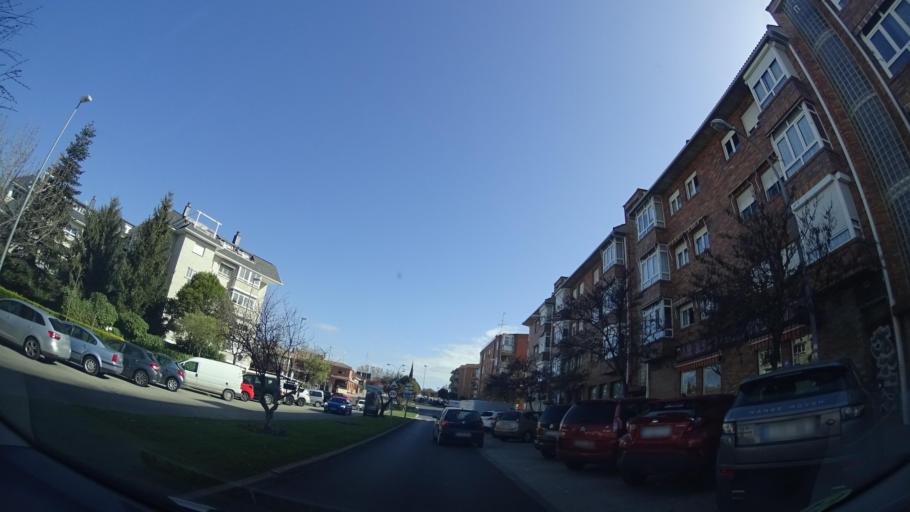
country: ES
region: Madrid
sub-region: Provincia de Madrid
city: Colmenar Viejo
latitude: 40.6632
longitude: -3.7748
